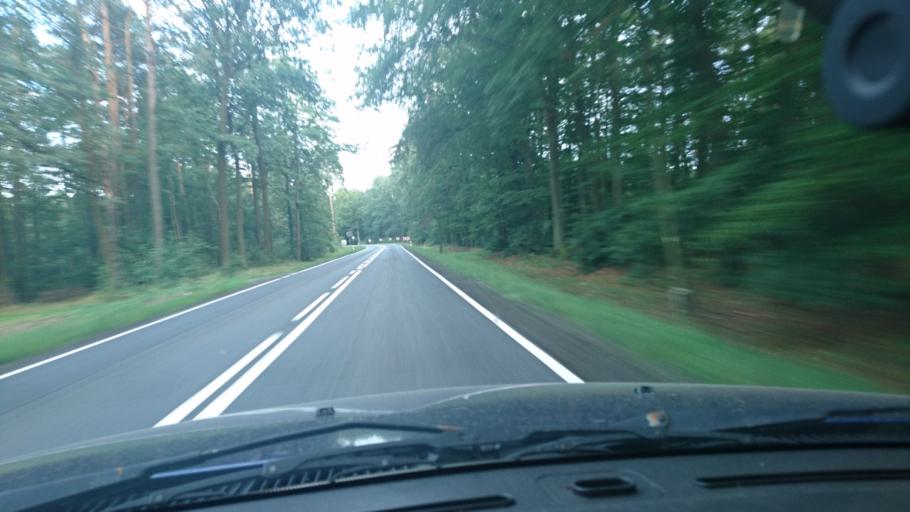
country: PL
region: Opole Voivodeship
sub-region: Powiat oleski
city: Olesno
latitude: 50.8512
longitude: 18.4683
